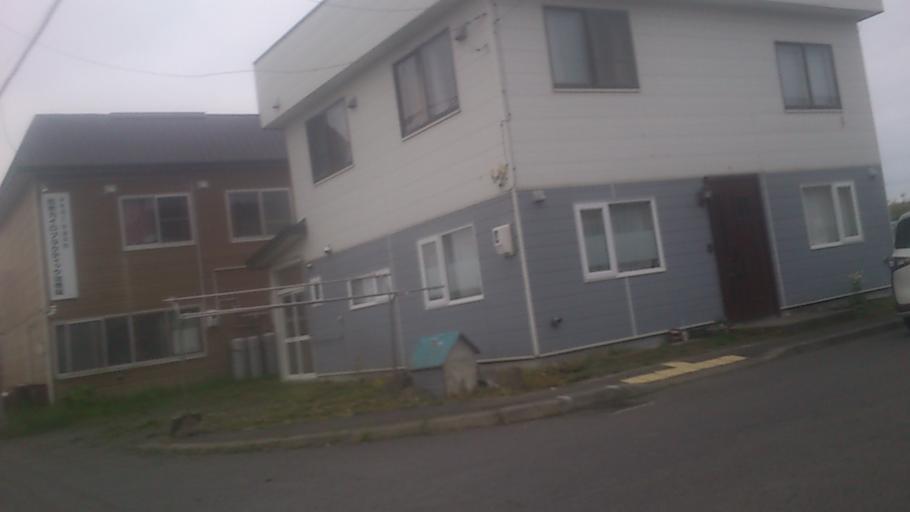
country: JP
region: Hokkaido
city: Kushiro
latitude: 42.9988
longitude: 144.4182
